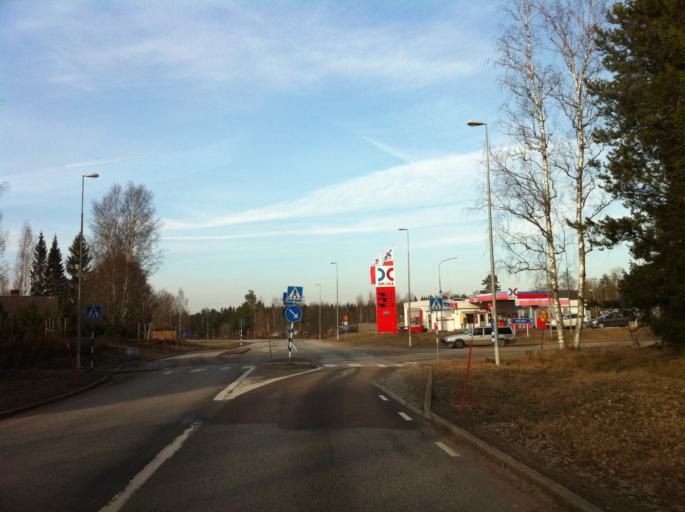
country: SE
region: Vaermland
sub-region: Storfors Kommun
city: Storfors
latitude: 59.5297
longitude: 14.2830
